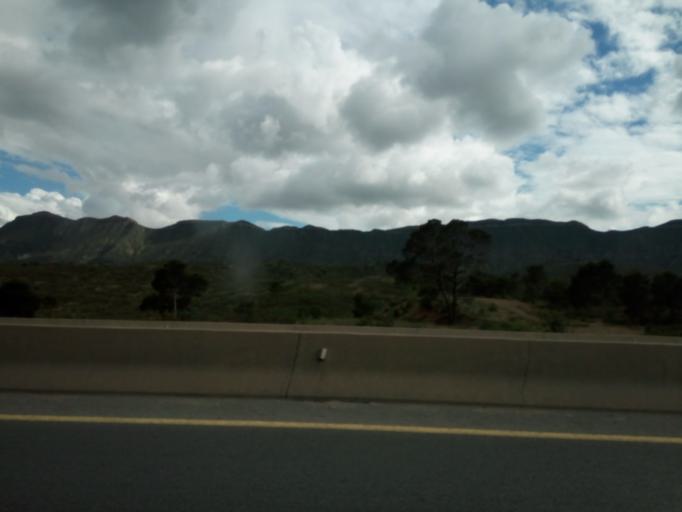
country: DZ
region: Bouira
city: Chorfa
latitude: 36.2457
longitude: 4.3033
